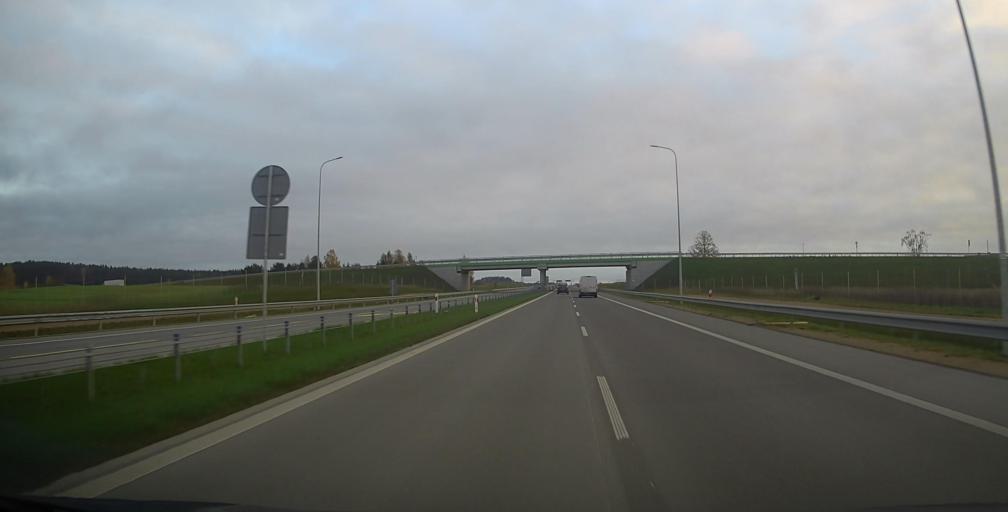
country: PL
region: Podlasie
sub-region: Powiat lomzynski
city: Piatnica
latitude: 53.2546
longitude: 22.1108
